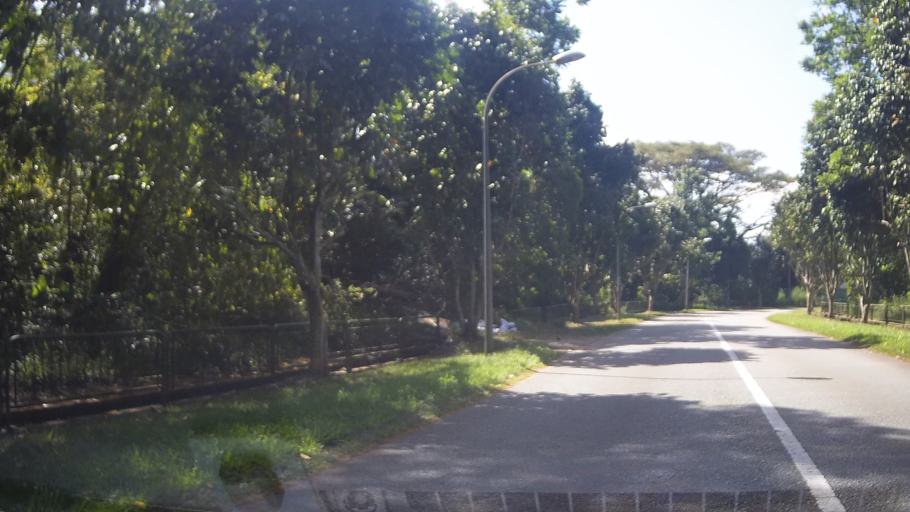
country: MY
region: Johor
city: Johor Bahru
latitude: 1.4353
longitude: 103.7191
